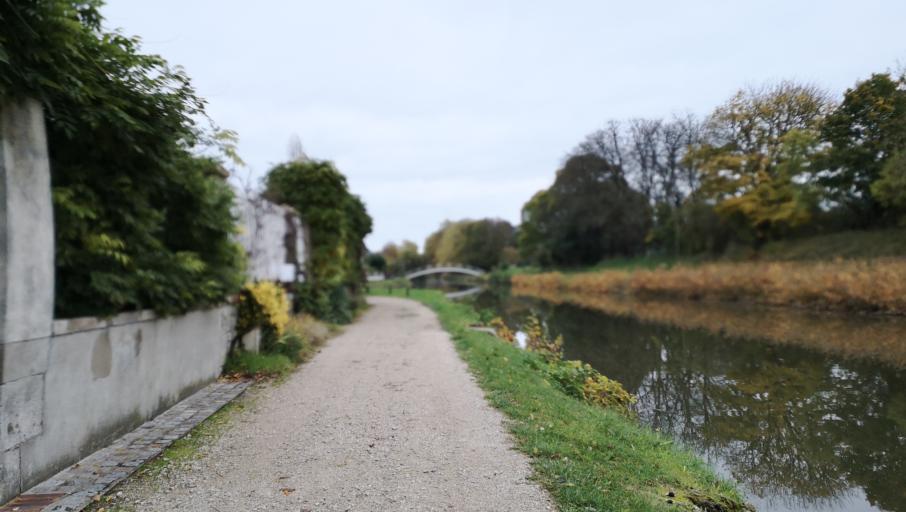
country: FR
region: Centre
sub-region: Departement du Loiret
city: Saint-Jean-de-Braye
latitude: 47.8990
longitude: 1.9867
